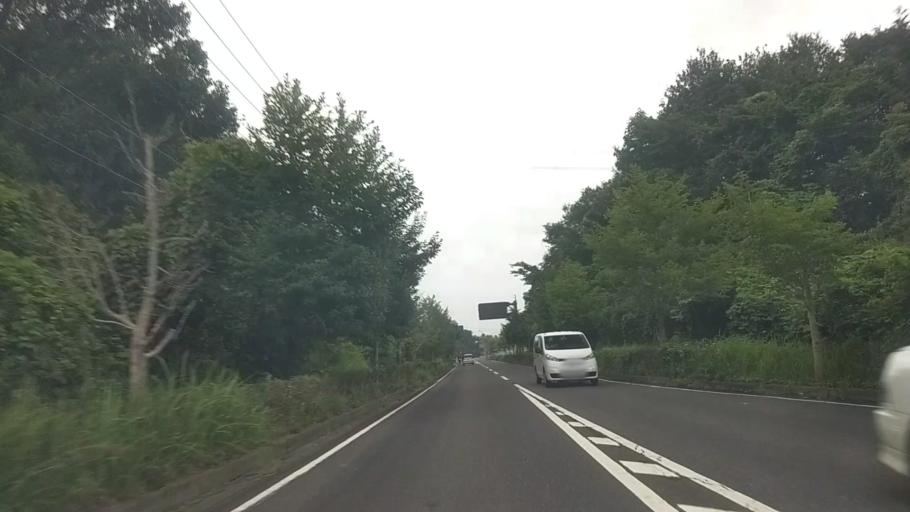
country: JP
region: Chiba
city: Kisarazu
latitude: 35.3860
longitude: 140.0022
